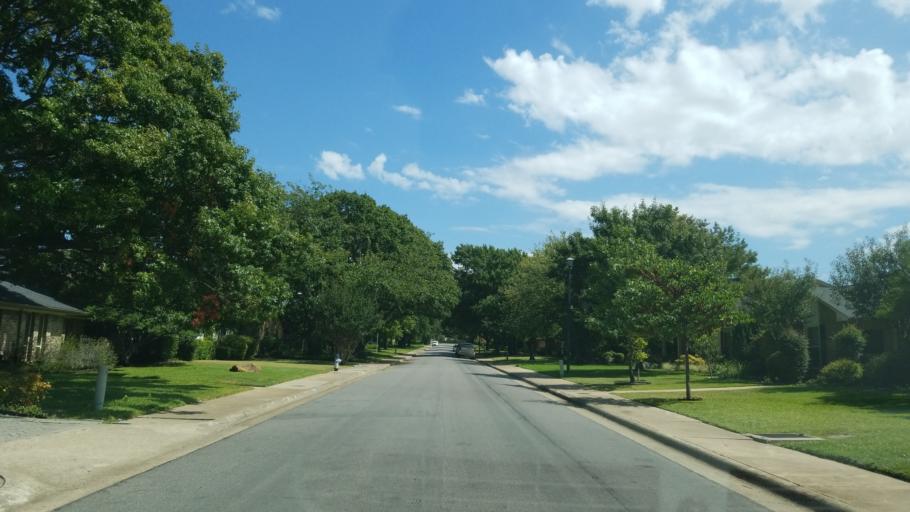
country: US
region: Texas
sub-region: Dallas County
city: Addison
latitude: 32.9671
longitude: -96.7821
